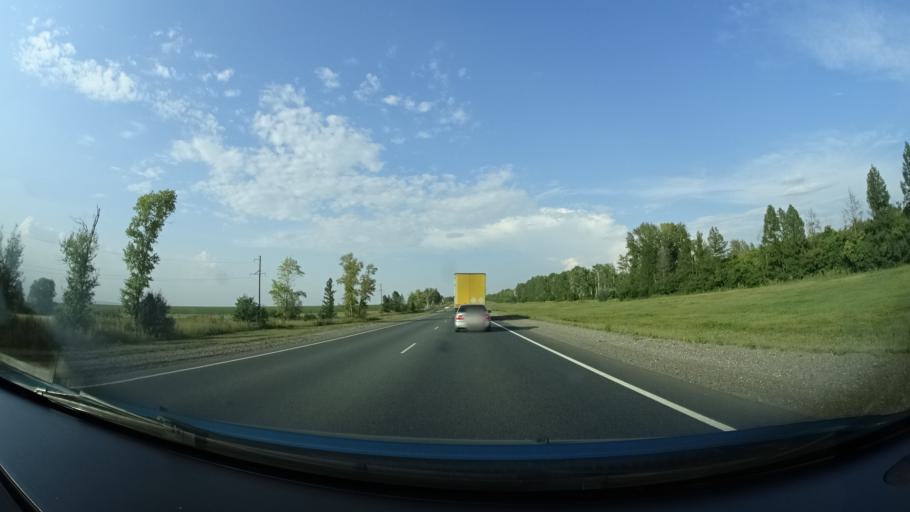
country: RU
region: Samara
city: Krasnyy Yar
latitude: 53.6568
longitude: 50.7495
